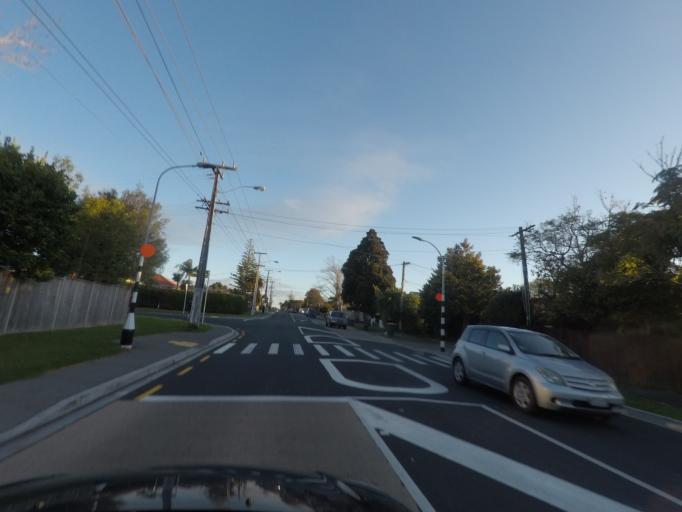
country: NZ
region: Auckland
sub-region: Auckland
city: Rosebank
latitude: -36.8799
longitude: 174.6463
